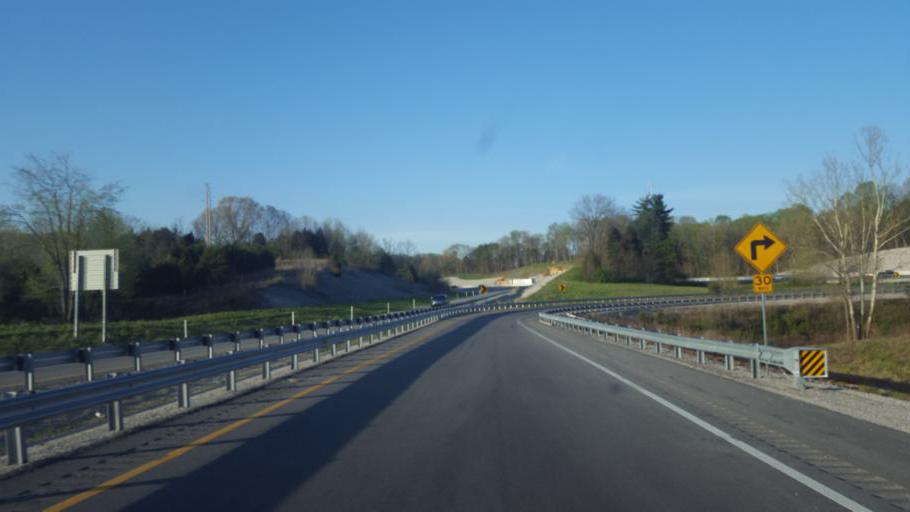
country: US
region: Kentucky
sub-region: Hart County
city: Munfordville
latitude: 37.2948
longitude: -85.9039
